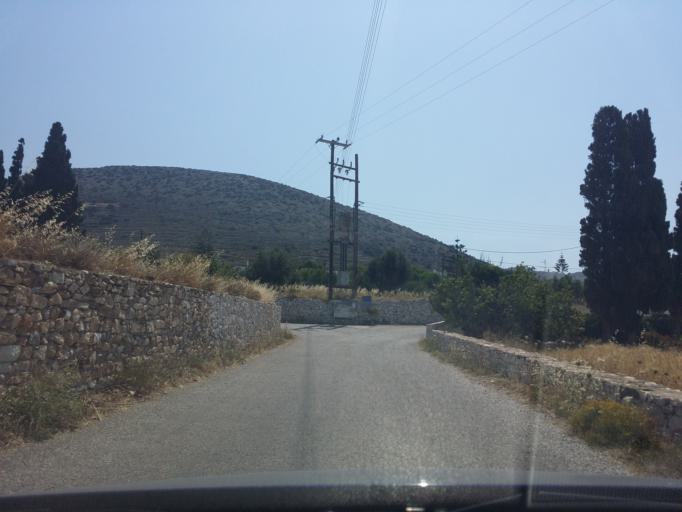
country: GR
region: South Aegean
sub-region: Nomos Kykladon
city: Antiparos
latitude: 37.0147
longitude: 25.1469
